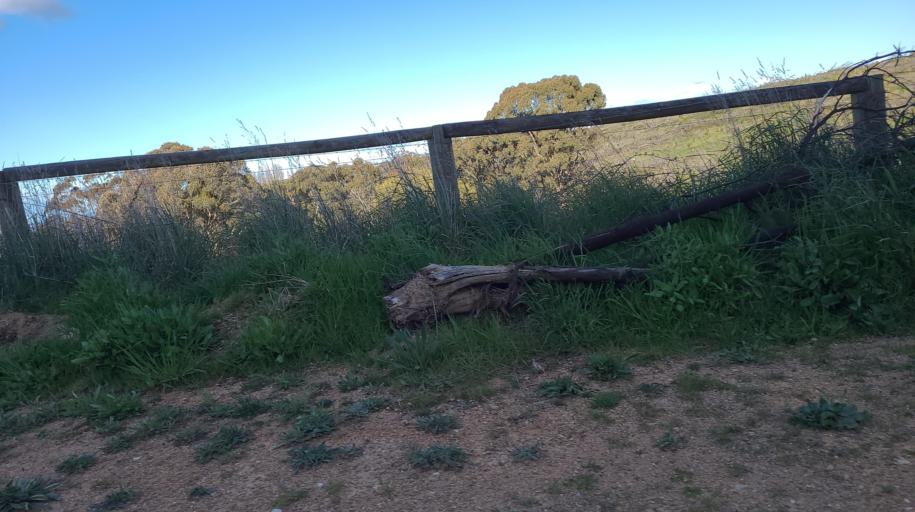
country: AU
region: New South Wales
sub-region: Blayney
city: Millthorpe
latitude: -33.4036
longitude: 149.3128
